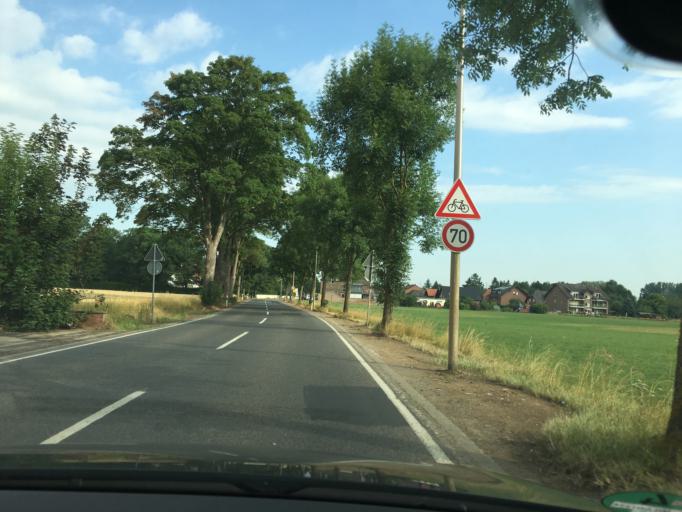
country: DE
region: North Rhine-Westphalia
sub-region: Regierungsbezirk Koln
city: Inden
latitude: 50.8936
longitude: 6.3612
